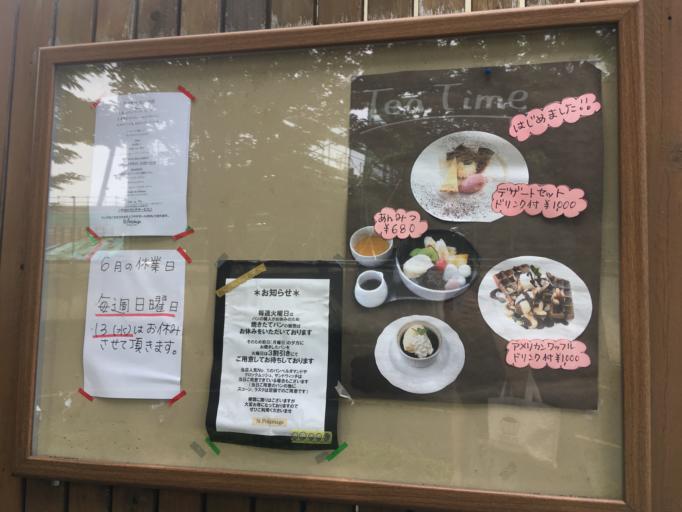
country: JP
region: Kanagawa
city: Minami-rinkan
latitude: 35.5086
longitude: 139.4699
